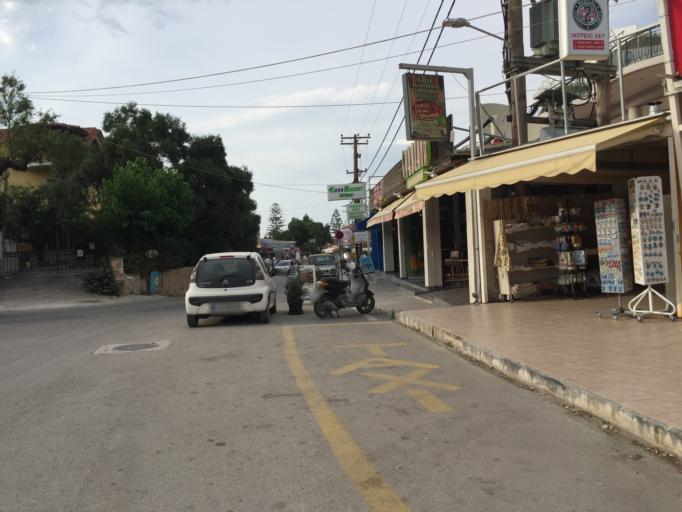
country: GR
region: Ionian Islands
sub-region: Nomos Zakynthou
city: Gaitanion
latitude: 37.8123
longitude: 20.8721
